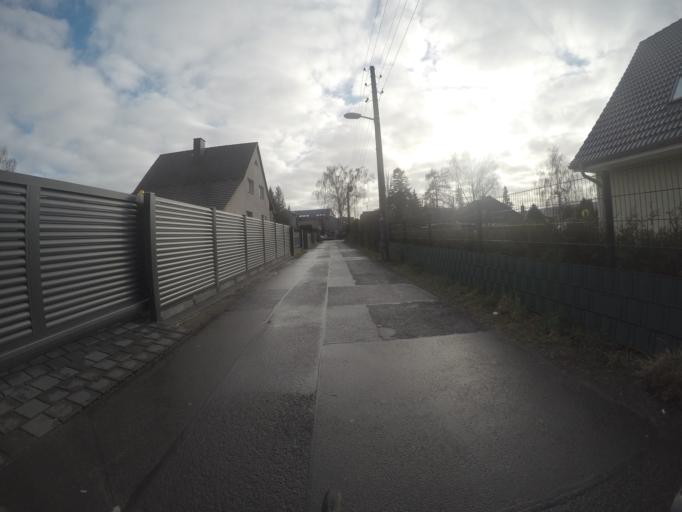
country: DE
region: Berlin
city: Falkenberg
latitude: 52.5699
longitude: 13.5561
